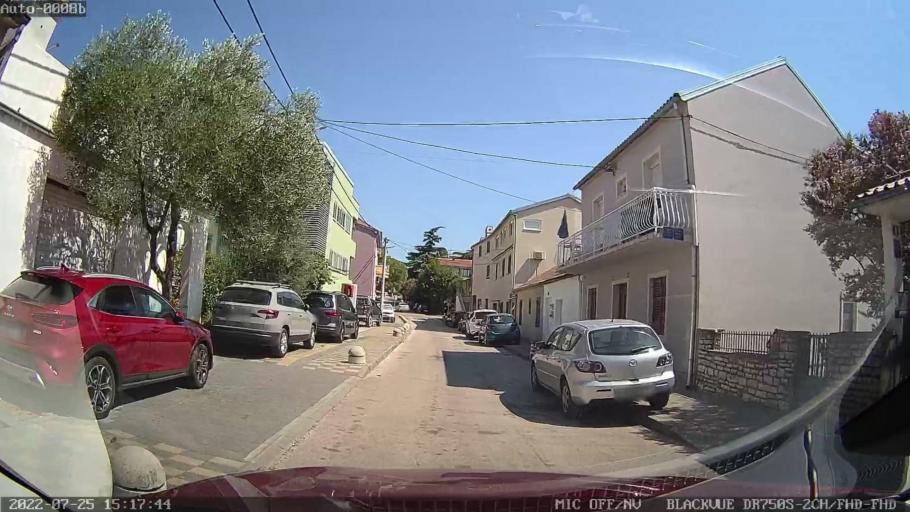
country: HR
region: Zadarska
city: Biograd na Moru
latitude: 43.9364
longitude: 15.4441
